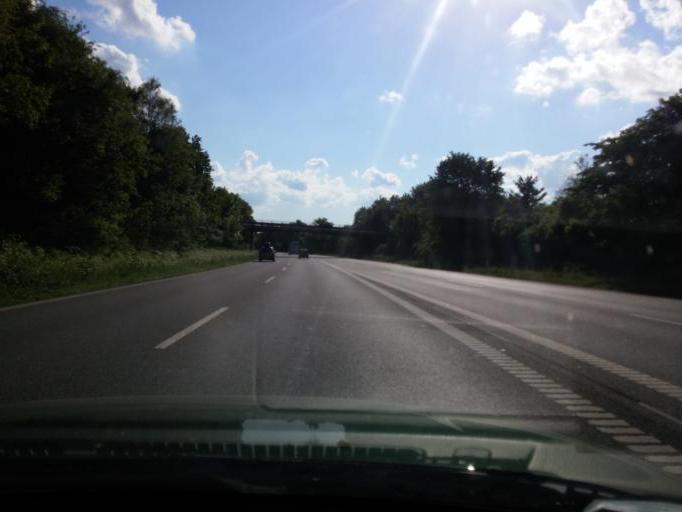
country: DK
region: South Denmark
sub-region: Kolding Kommune
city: Kolding
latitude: 55.5459
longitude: 9.5256
